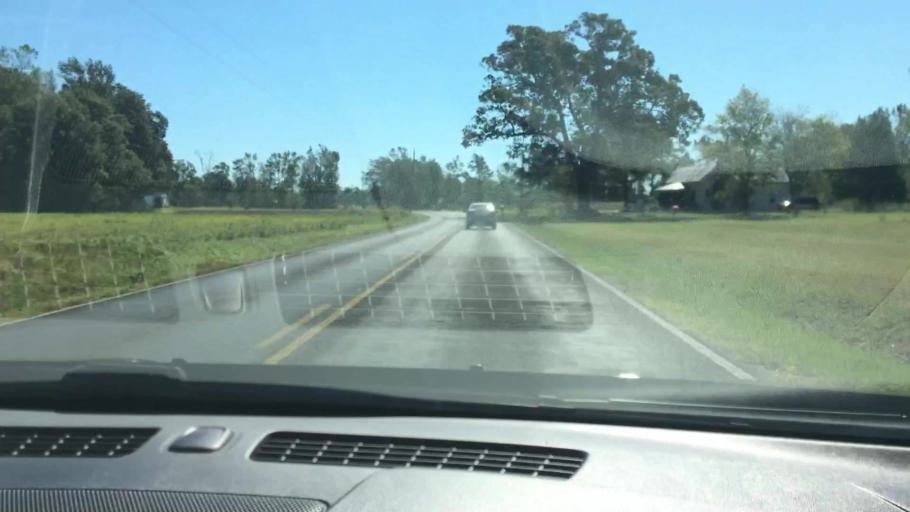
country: US
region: North Carolina
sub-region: Pitt County
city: Grifton
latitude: 35.3674
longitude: -77.3520
